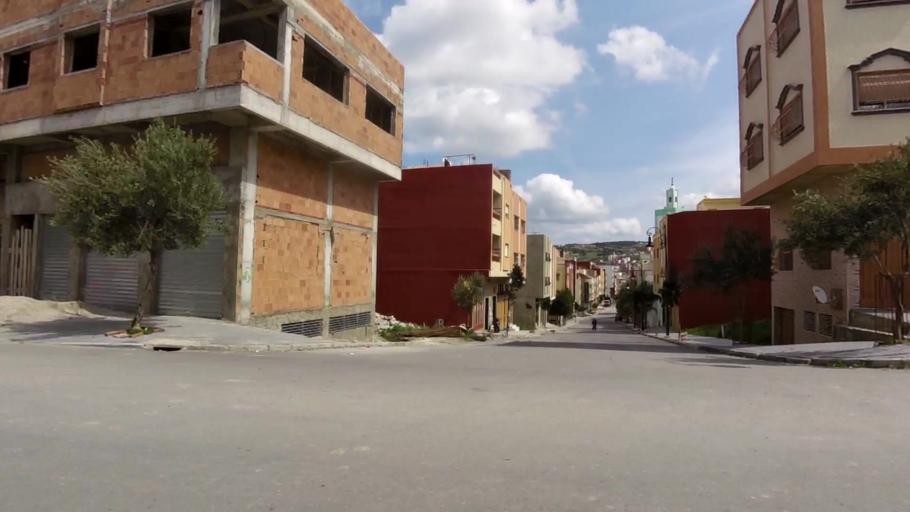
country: MA
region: Tanger-Tetouan
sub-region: Tanger-Assilah
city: Tangier
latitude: 35.7618
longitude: -5.7613
